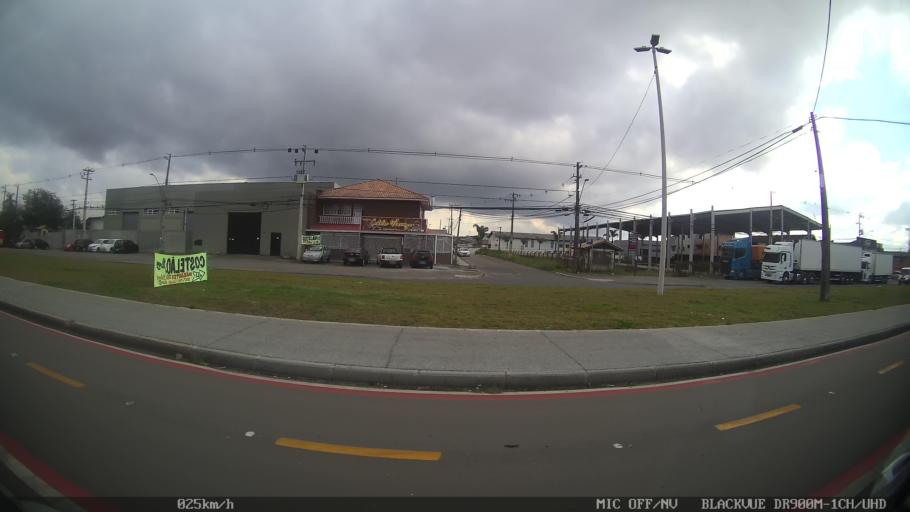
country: BR
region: Parana
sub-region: Pinhais
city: Pinhais
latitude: -25.4159
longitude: -49.1905
